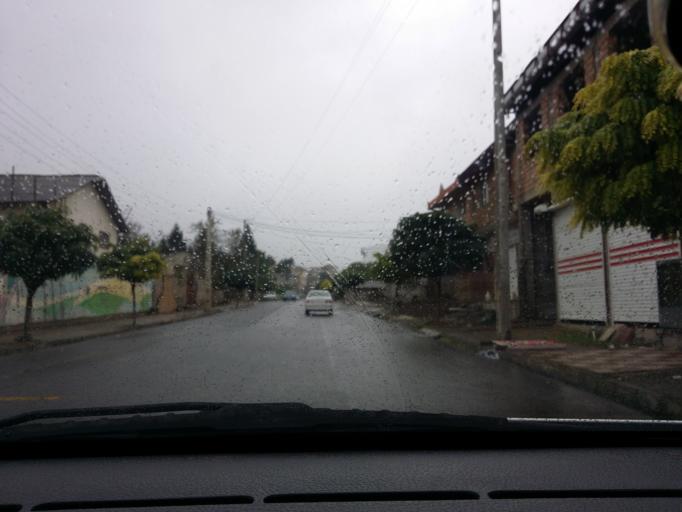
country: IR
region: Mazandaran
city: Chalus
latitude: 36.5270
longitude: 51.2310
